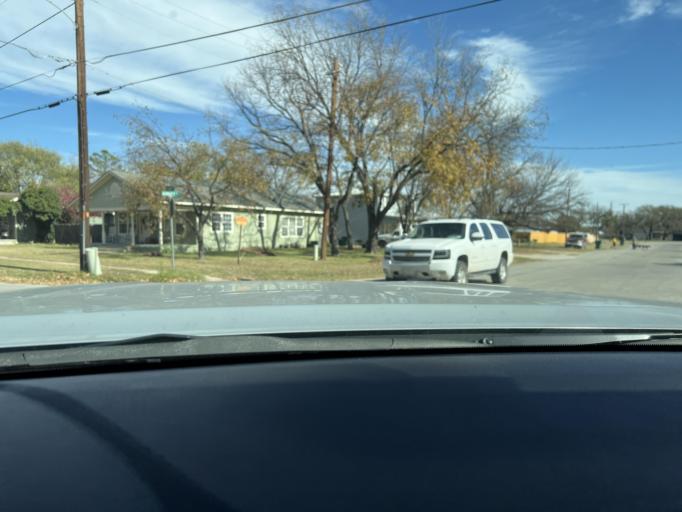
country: US
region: Texas
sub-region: Eastland County
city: Eastland
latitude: 32.3891
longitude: -98.8182
